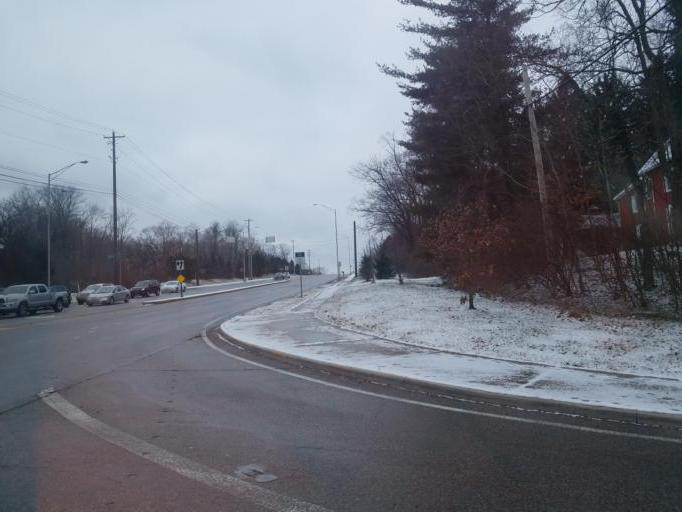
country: US
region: Ohio
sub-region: Franklin County
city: Worthington
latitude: 40.1166
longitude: -83.0350
